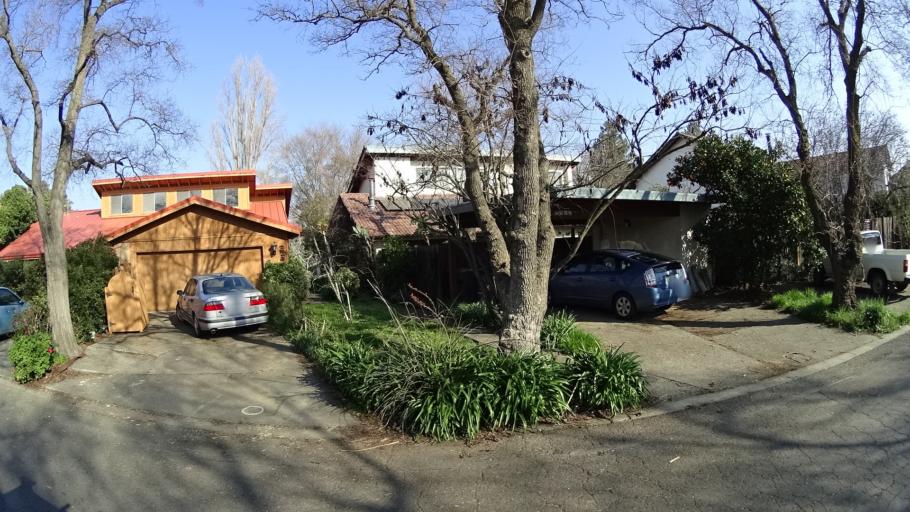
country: US
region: California
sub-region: Yolo County
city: Davis
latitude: 38.5506
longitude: -121.7815
